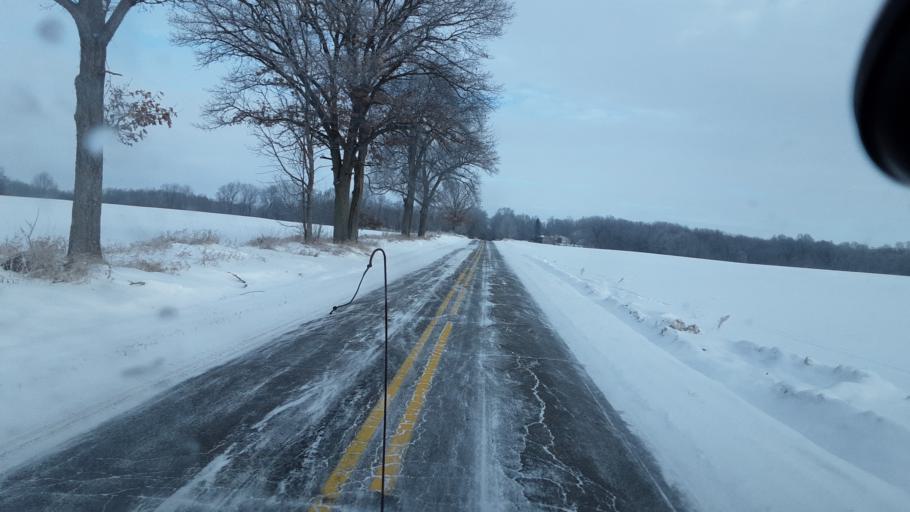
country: US
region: Michigan
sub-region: Ingham County
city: Leslie
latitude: 42.3573
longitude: -84.4826
